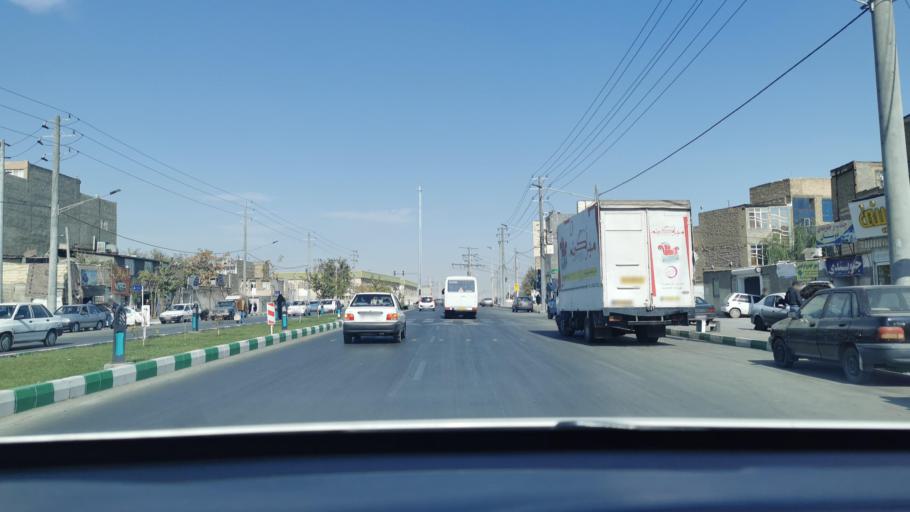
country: IR
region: Razavi Khorasan
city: Mashhad
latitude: 36.3396
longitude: 59.6079
